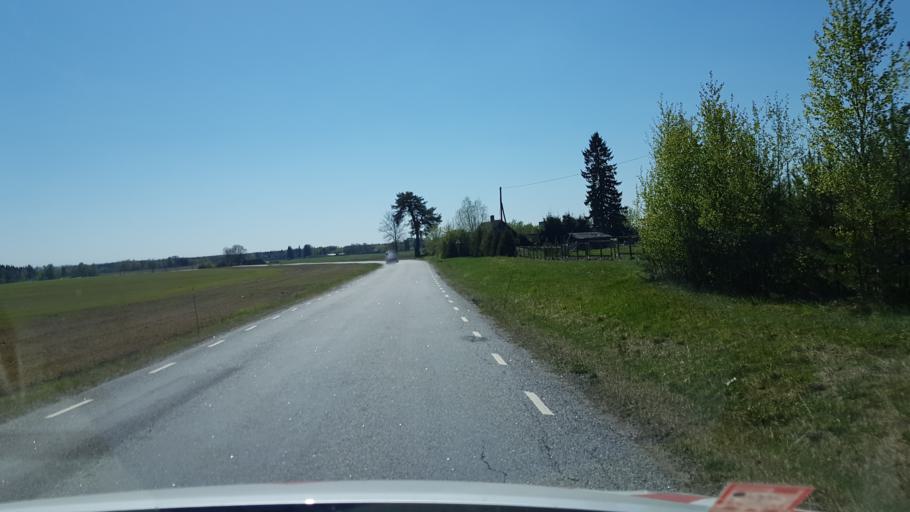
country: EE
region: Vorumaa
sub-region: Voru linn
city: Voru
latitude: 57.9245
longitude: 26.9512
